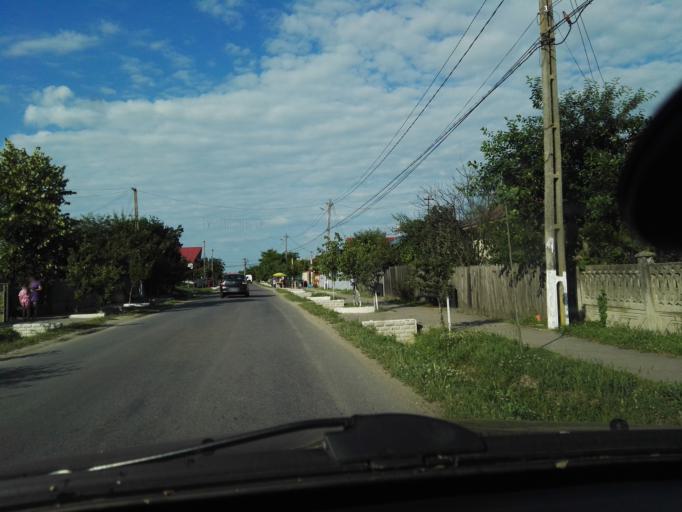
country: RO
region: Giurgiu
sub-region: Comuna Comana
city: Gradistea
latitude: 44.2129
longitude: 26.1579
